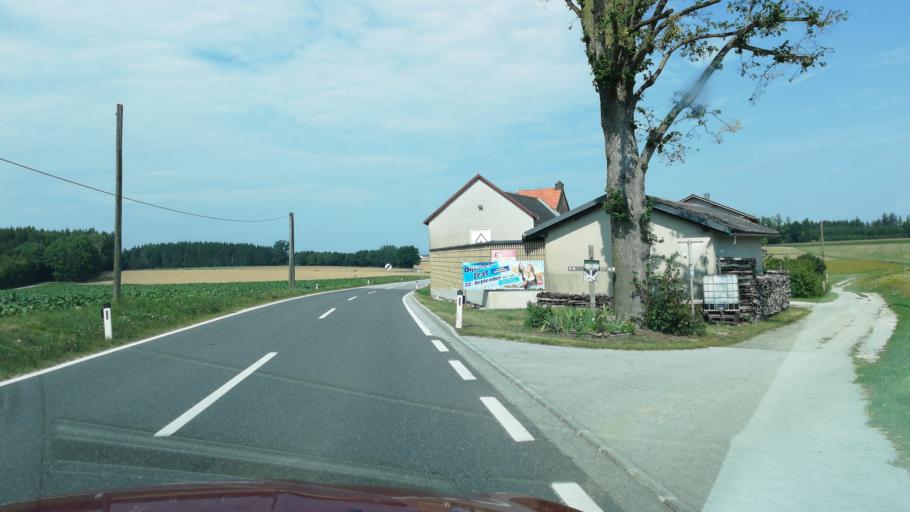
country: AT
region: Upper Austria
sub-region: Politischer Bezirk Steyr-Land
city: Sierning
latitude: 48.0590
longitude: 14.3156
